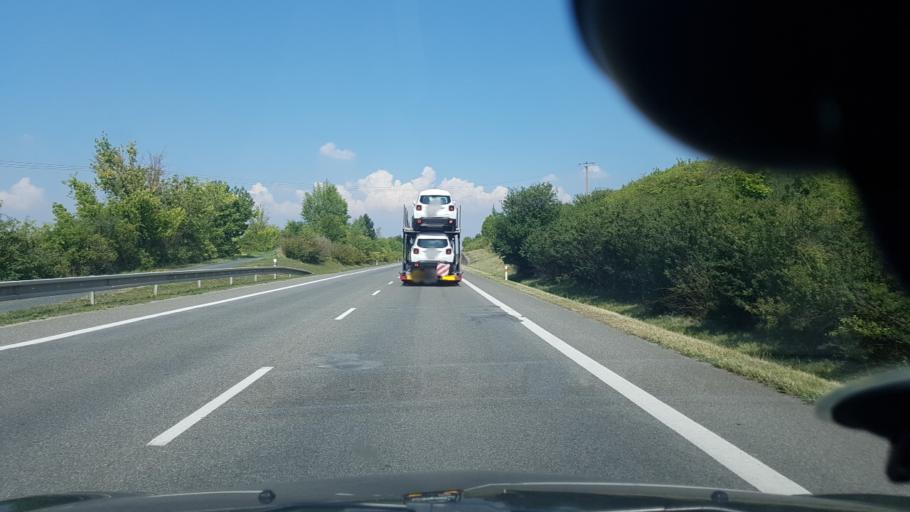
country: CZ
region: South Moravian
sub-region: Okres Breclav
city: Mikulov
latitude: 48.8239
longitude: 16.6159
